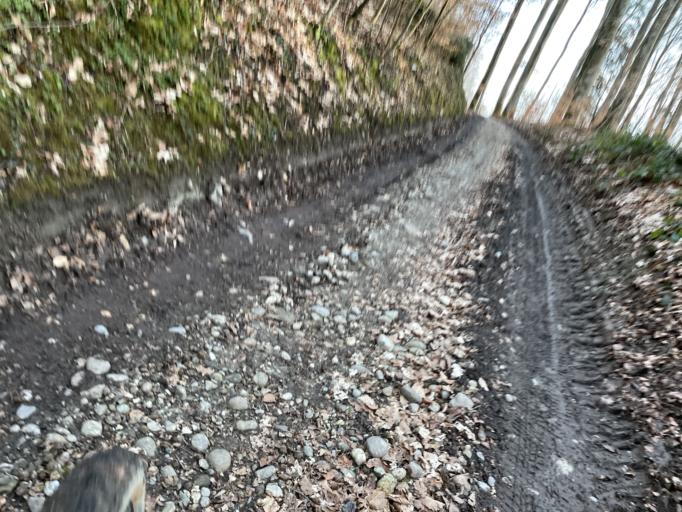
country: CH
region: Bern
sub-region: Bern-Mittelland District
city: Toffen
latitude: 46.8491
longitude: 7.5110
